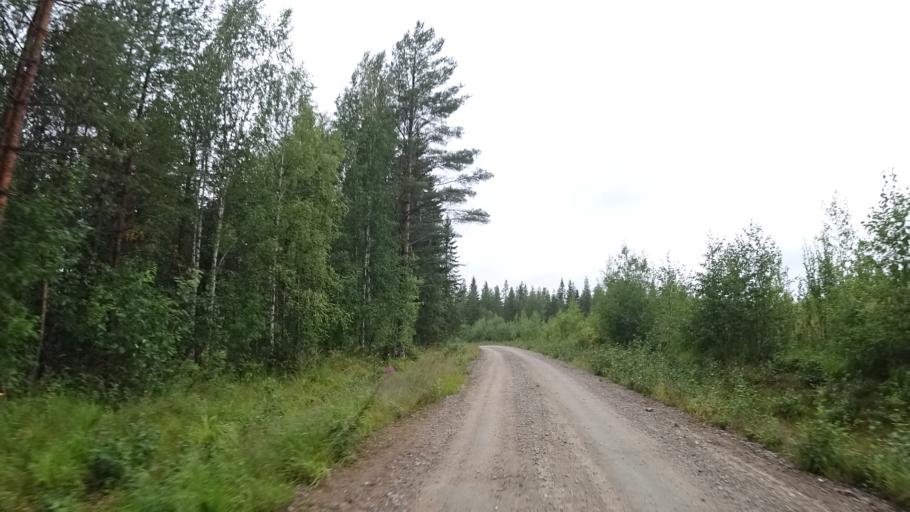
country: FI
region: North Karelia
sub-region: Pielisen Karjala
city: Lieksa
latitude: 63.5066
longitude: 30.1528
